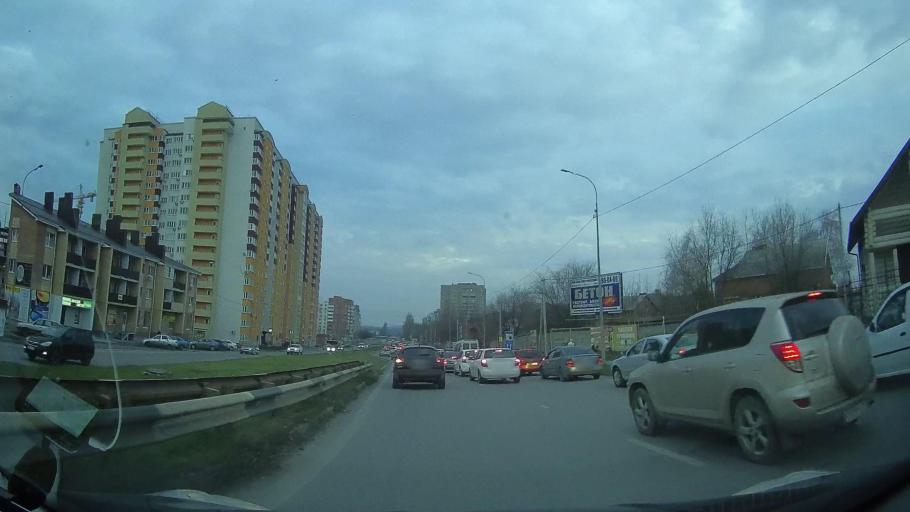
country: RU
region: Rostov
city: Severnyy
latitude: 47.3049
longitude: 39.7223
